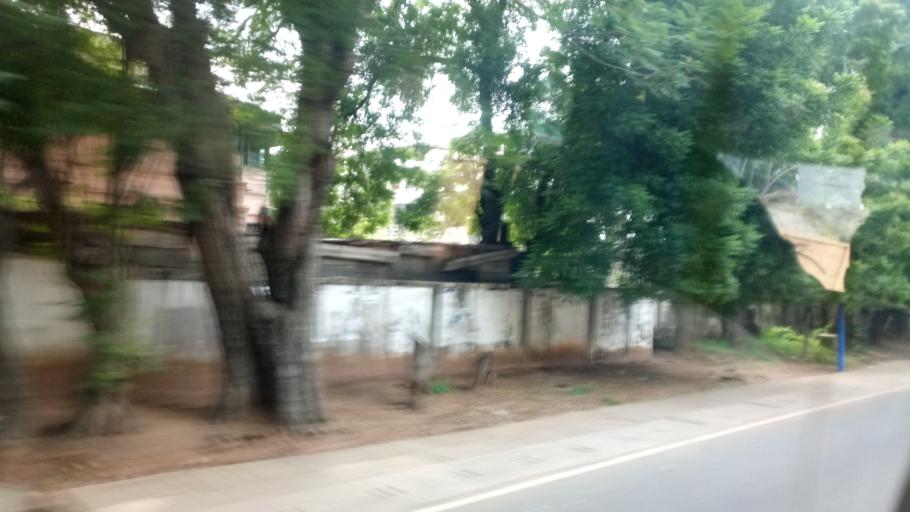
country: GH
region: Greater Accra
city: Accra
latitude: 5.5562
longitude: -0.1938
